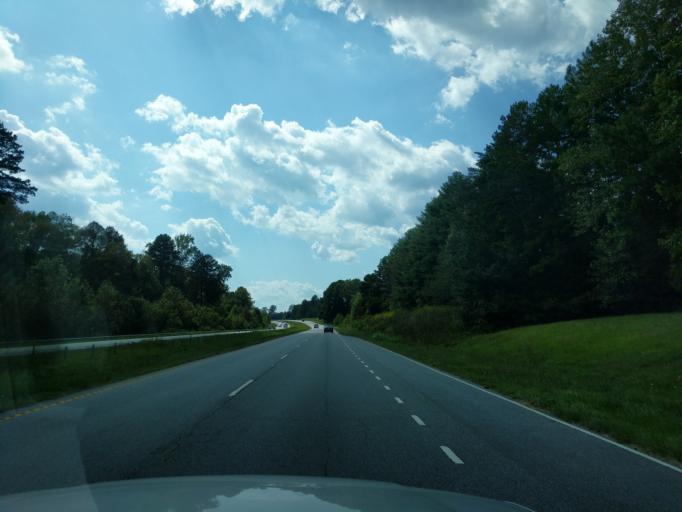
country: US
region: South Carolina
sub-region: Pickens County
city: Liberty
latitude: 34.7941
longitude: -82.6476
